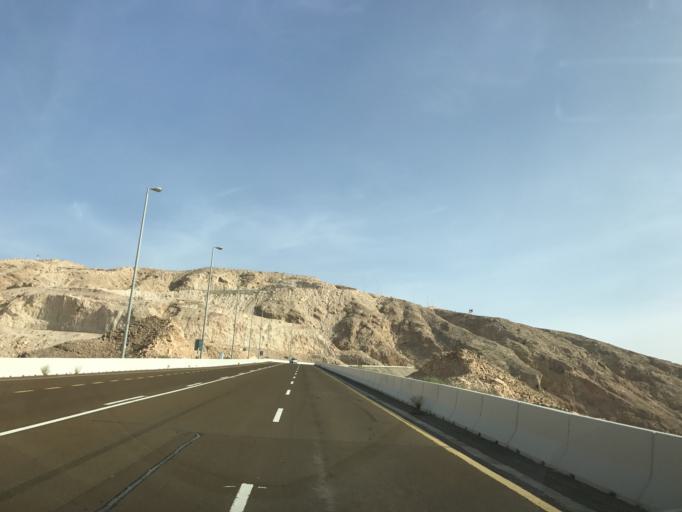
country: AE
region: Abu Dhabi
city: Al Ain
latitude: 24.0893
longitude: 55.7631
